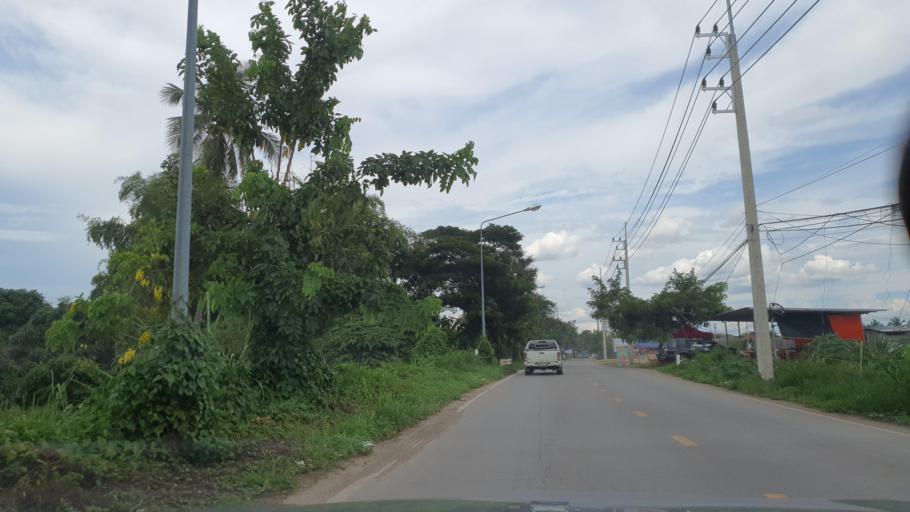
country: TH
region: Chiang Mai
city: Mae Wang
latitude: 18.6048
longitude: 98.7930
